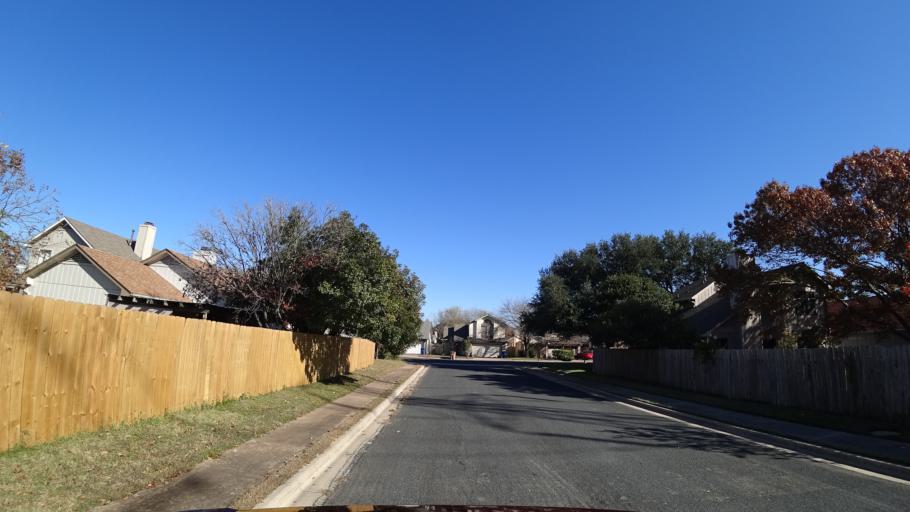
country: US
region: Texas
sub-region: Travis County
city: Wells Branch
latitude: 30.4189
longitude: -97.6884
